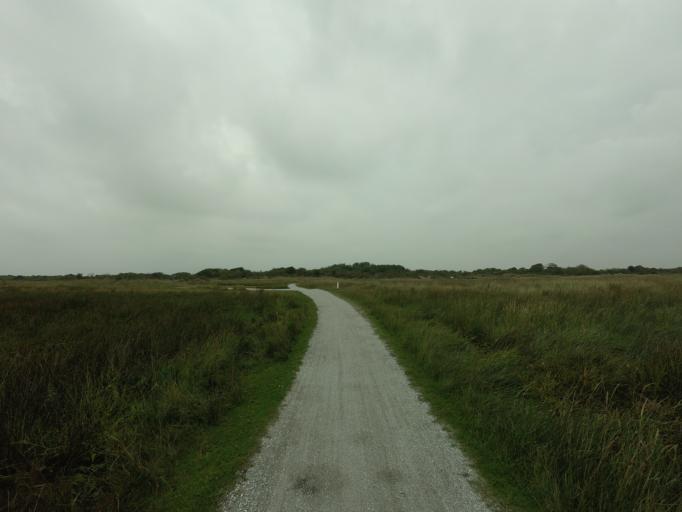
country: NL
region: Friesland
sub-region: Gemeente Schiermonnikoog
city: Schiermonnikoog
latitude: 53.4858
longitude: 6.2180
